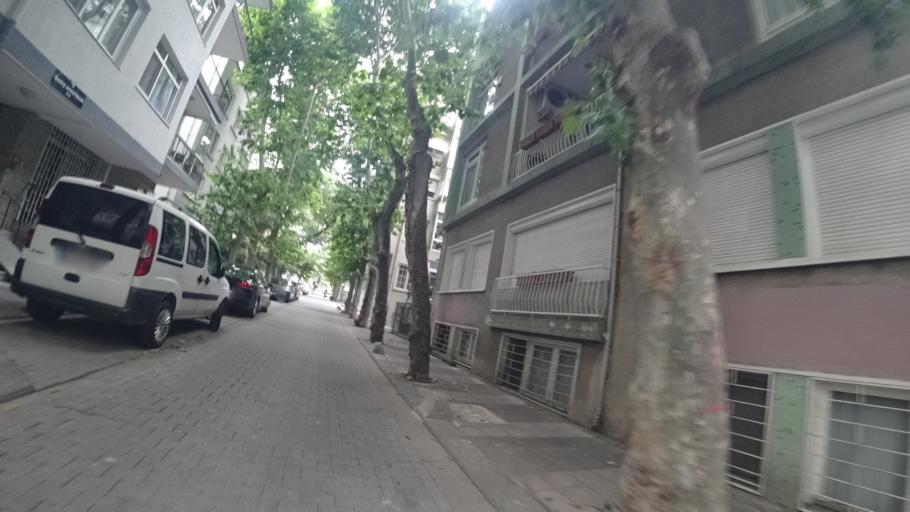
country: TR
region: Istanbul
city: UEskuedar
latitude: 40.9801
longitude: 29.0228
